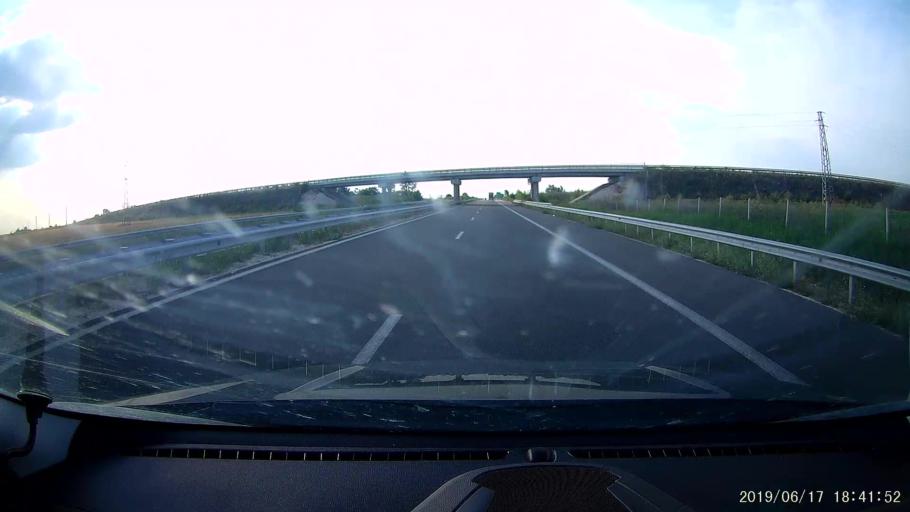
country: BG
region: Stara Zagora
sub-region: Obshtina Chirpan
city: Chirpan
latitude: 42.1804
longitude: 25.2477
